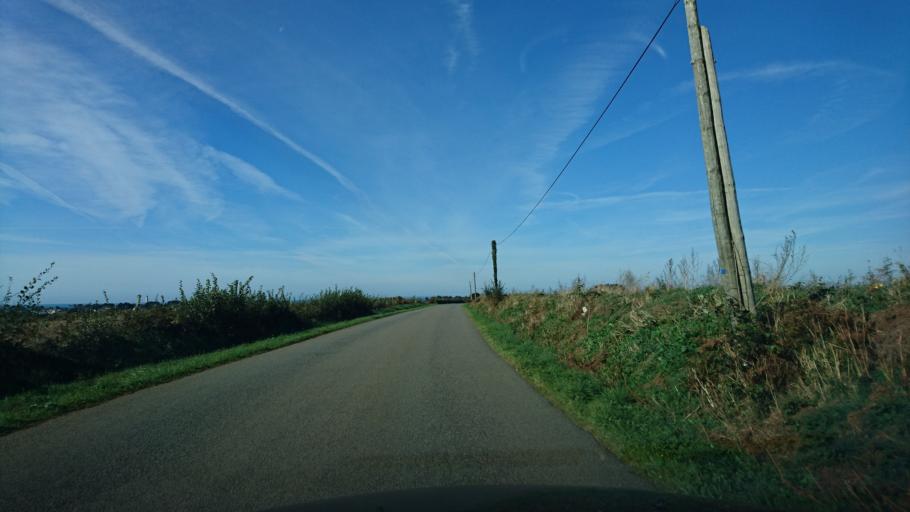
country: FR
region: Brittany
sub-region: Departement du Finistere
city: Plouarzel
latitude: 48.4278
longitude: -4.7516
